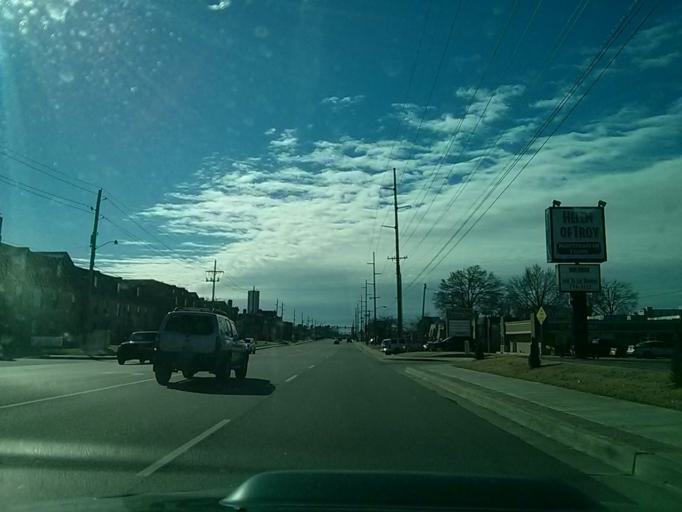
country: US
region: Oklahoma
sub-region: Tulsa County
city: Jenks
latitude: 36.0662
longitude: -95.9580
